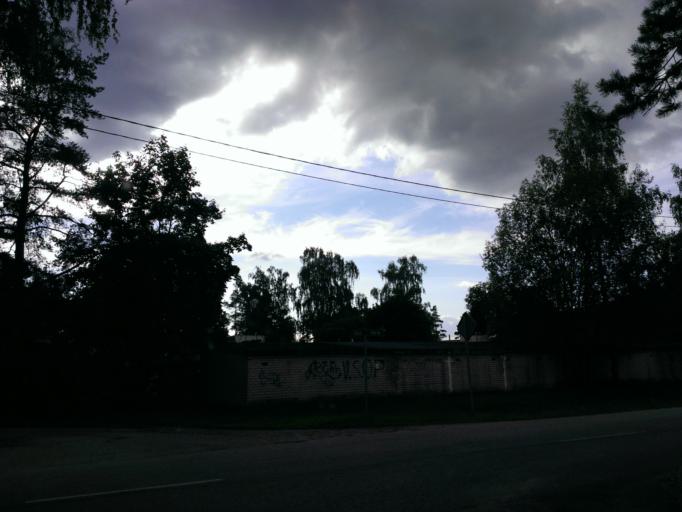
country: LV
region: Ikskile
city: Ikskile
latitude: 56.8368
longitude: 24.4876
